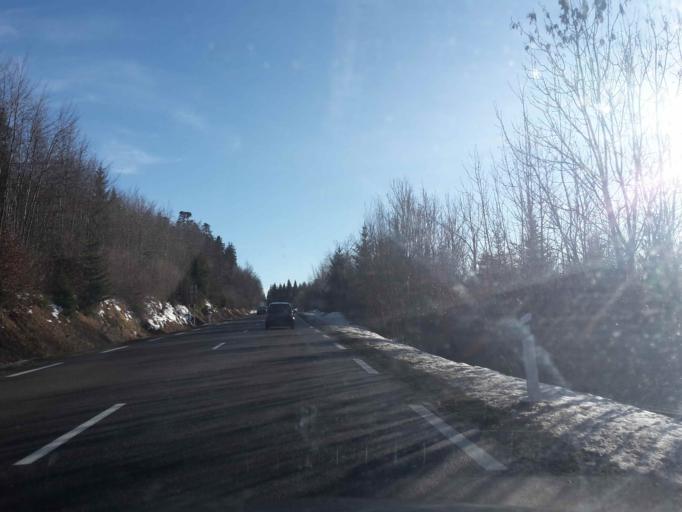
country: FR
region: Franche-Comte
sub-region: Departement du Doubs
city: Doubs
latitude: 47.0055
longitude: 6.3266
